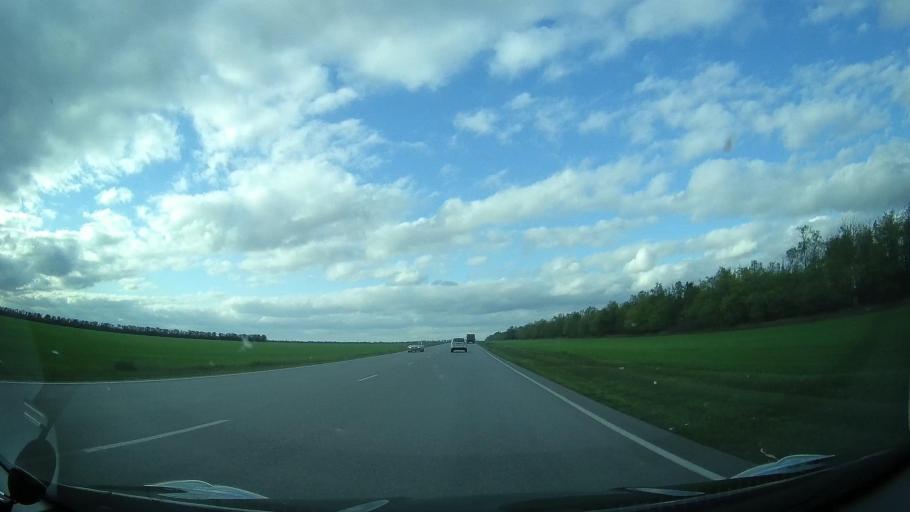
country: RU
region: Rostov
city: Kagal'nitskaya
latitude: 46.9115
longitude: 40.1131
